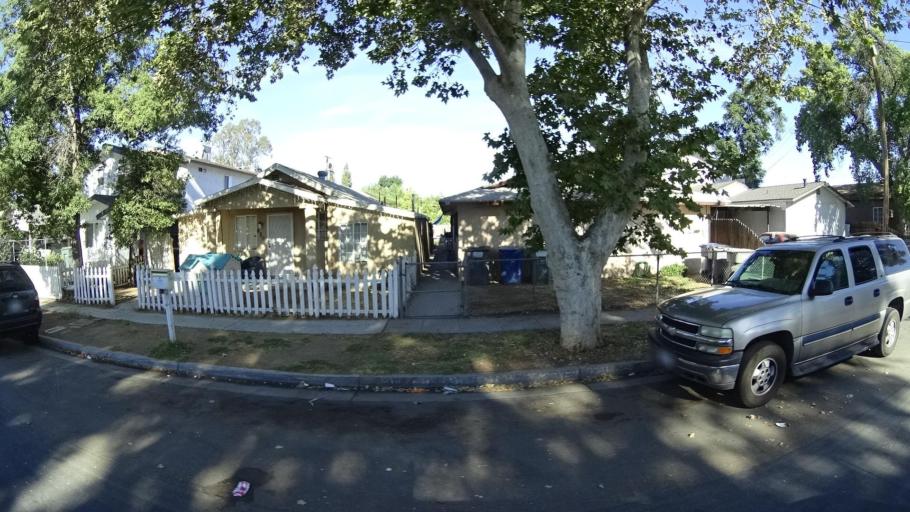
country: US
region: California
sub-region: Fresno County
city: Fresno
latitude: 36.7522
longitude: -119.7703
